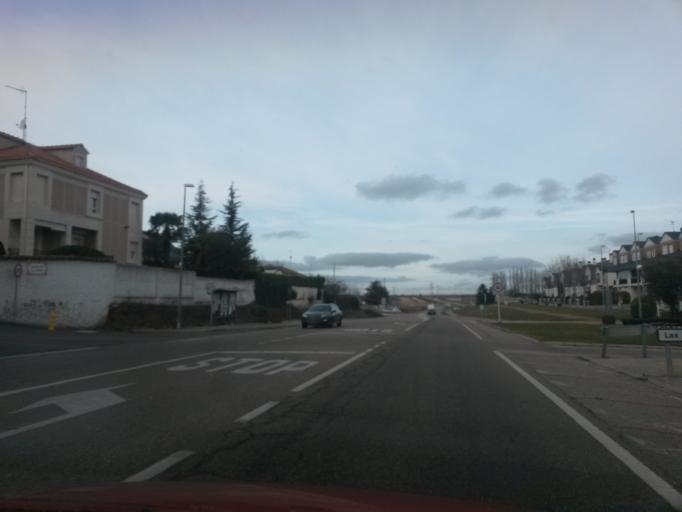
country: ES
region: Castille and Leon
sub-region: Provincia de Salamanca
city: Villares de la Reina
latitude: 40.9934
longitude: -5.6579
